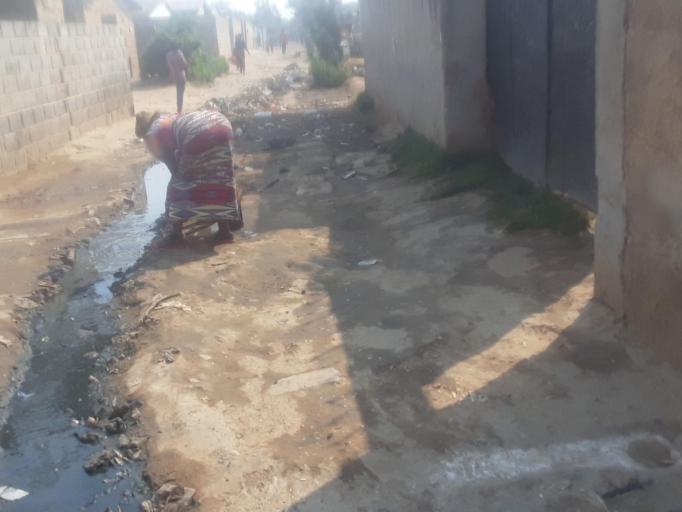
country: ZM
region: Lusaka
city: Lusaka
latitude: -15.3551
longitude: 28.2893
